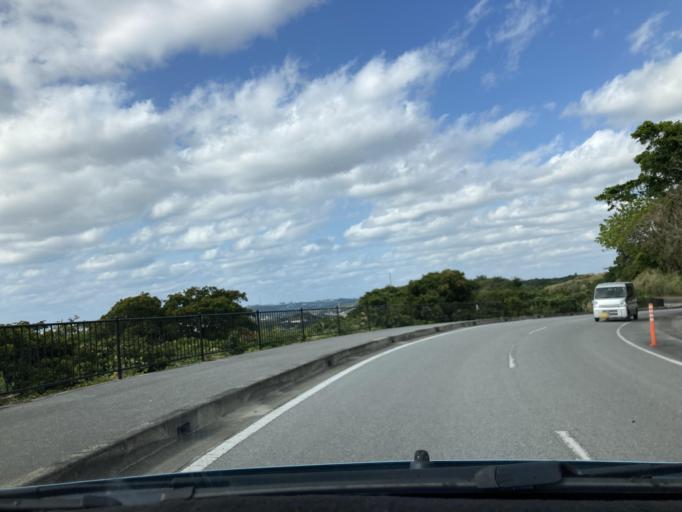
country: JP
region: Okinawa
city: Tomigusuku
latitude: 26.1713
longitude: 127.7600
